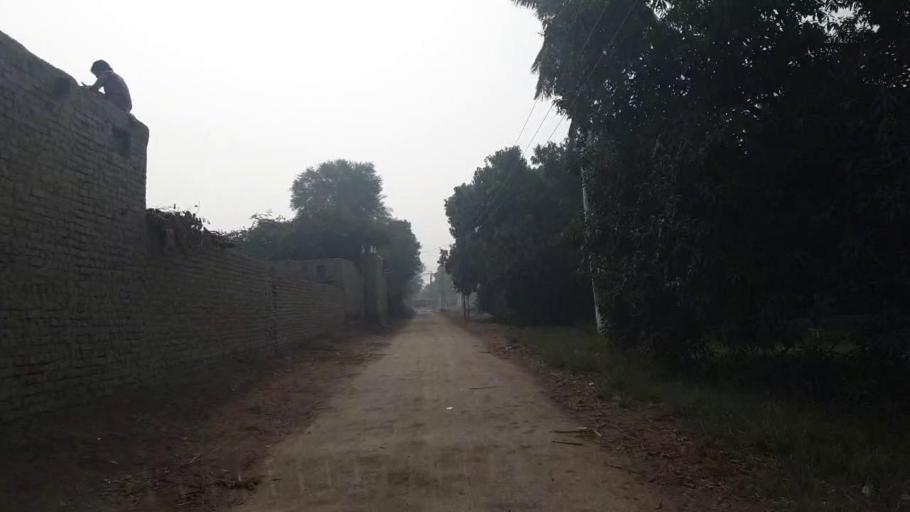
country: PK
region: Sindh
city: Tando Adam
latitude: 25.7842
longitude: 68.5962
